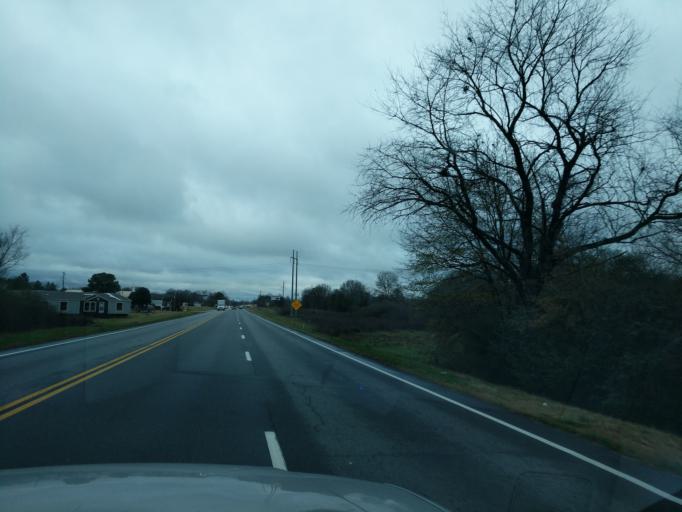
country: US
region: Georgia
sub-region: Franklin County
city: Lavonia
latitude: 34.4024
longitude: -83.1024
